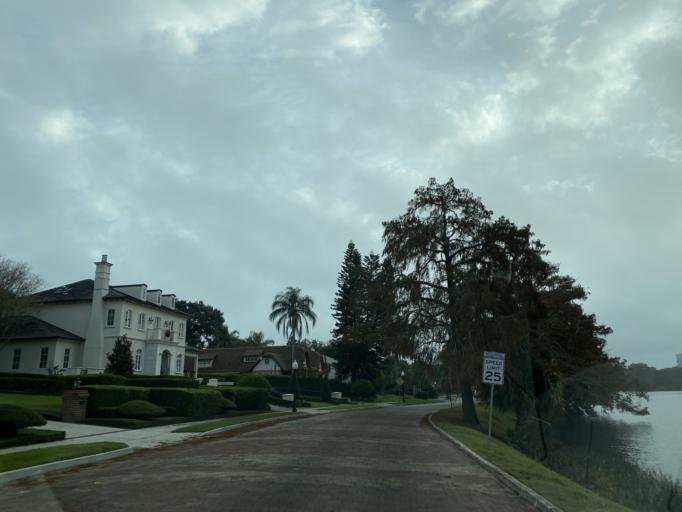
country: US
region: Florida
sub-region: Orange County
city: Orlando
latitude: 28.5610
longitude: -81.3931
